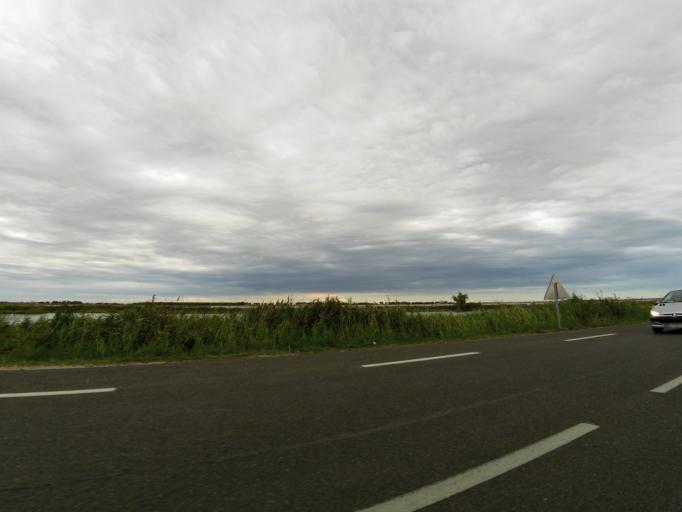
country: FR
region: Languedoc-Roussillon
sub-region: Departement du Gard
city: Le Grau-du-Roi
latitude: 43.5386
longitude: 4.1446
